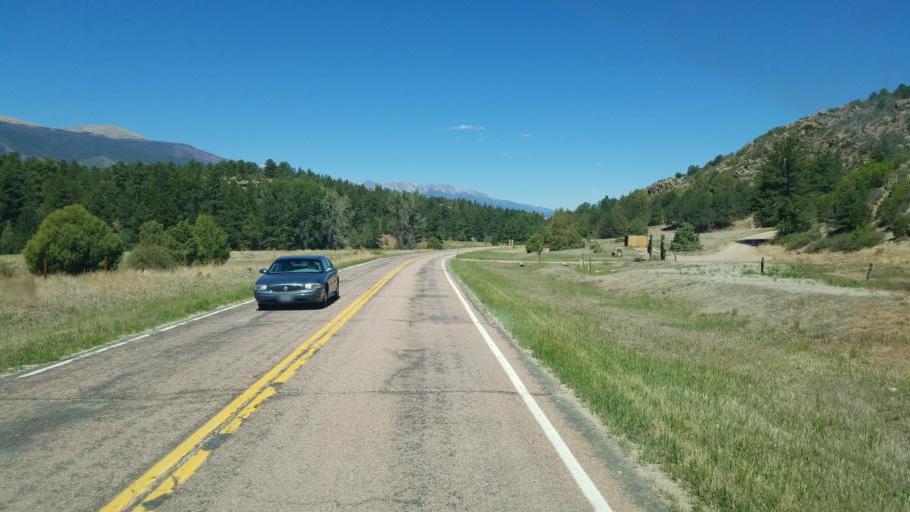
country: US
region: Colorado
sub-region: Custer County
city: Westcliffe
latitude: 38.2504
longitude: -105.5790
